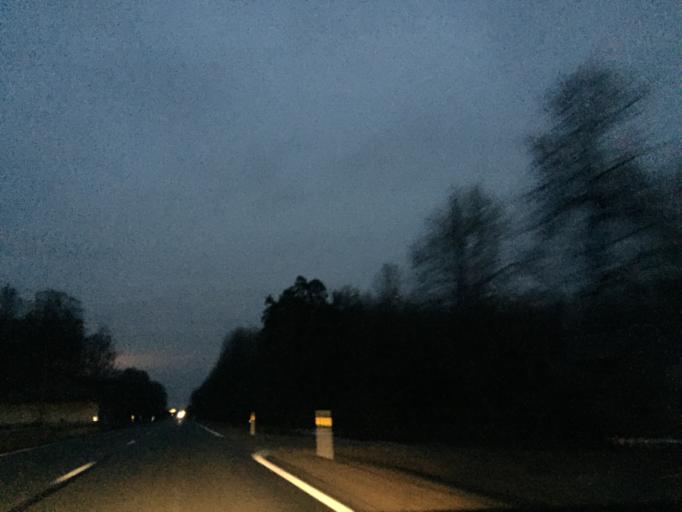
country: LT
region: Siauliu apskritis
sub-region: Joniskis
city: Joniskis
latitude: 56.3850
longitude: 23.6775
